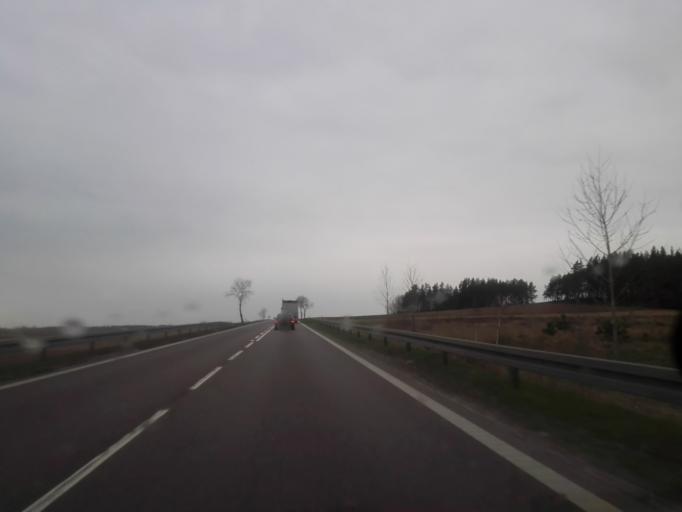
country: PL
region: Podlasie
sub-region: Powiat grajewski
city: Grajewo
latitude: 53.6158
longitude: 22.3876
